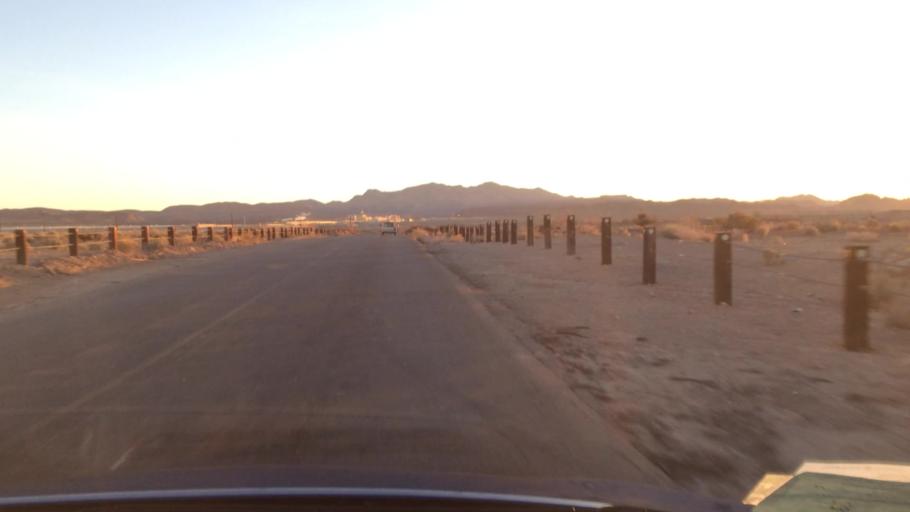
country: US
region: Nevada
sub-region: Clark County
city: Nellis Air Force Base
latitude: 36.2143
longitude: -114.8992
